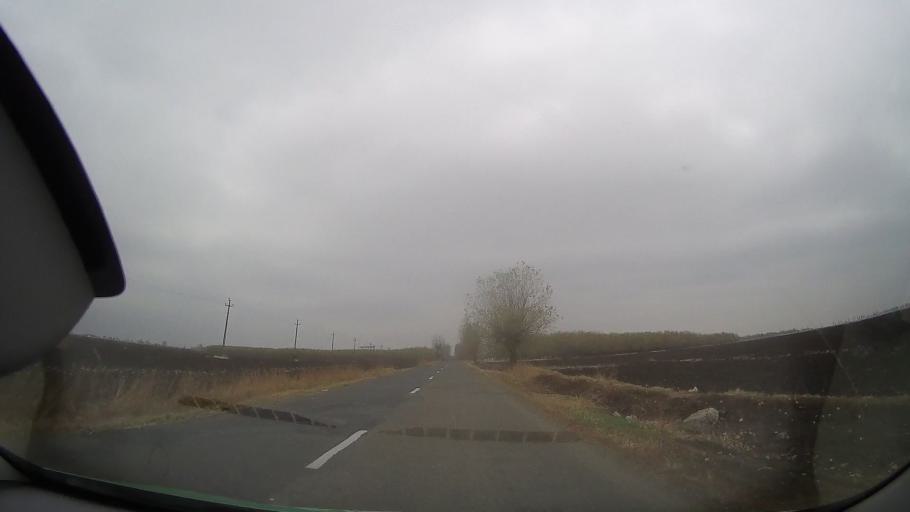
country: RO
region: Ialomita
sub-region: Comuna Grindu
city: Grindu
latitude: 44.7872
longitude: 26.9025
